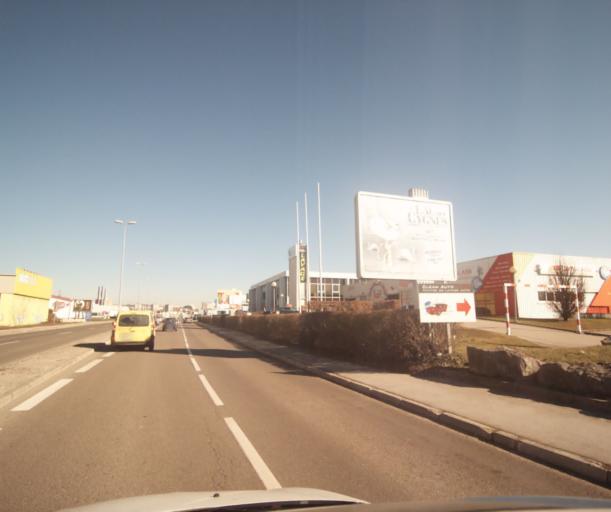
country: FR
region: Franche-Comte
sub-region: Departement du Doubs
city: Pirey
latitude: 47.2371
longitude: 5.9867
